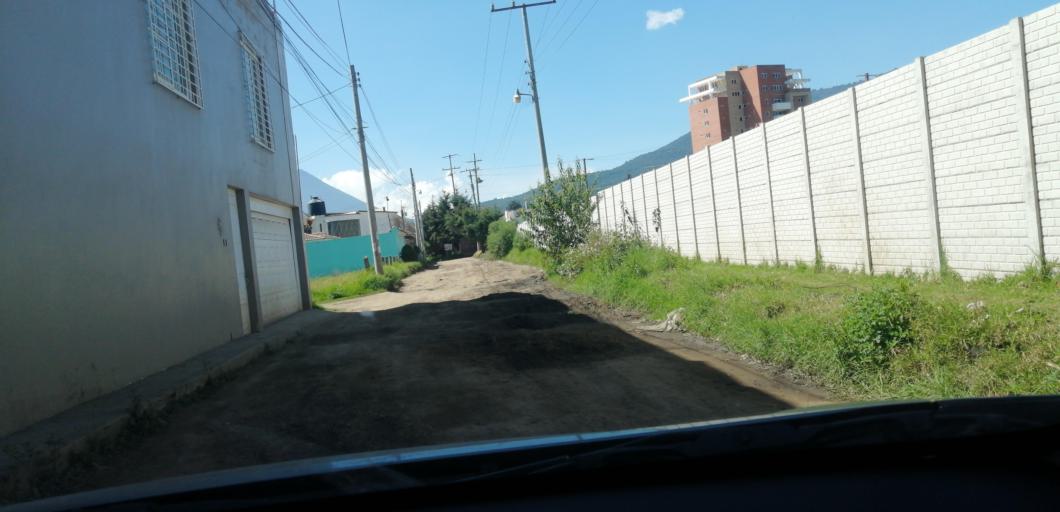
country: GT
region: Quetzaltenango
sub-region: Municipio de La Esperanza
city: La Esperanza
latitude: 14.8655
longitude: -91.5505
